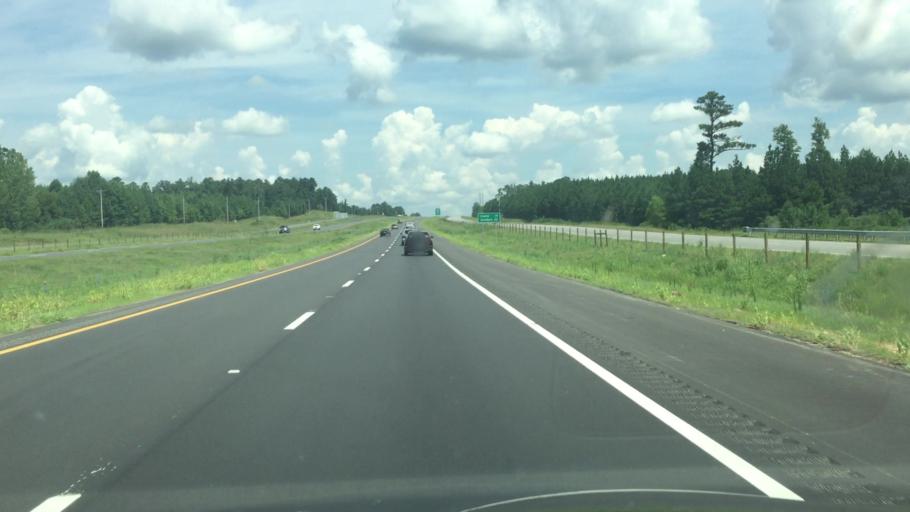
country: US
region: North Carolina
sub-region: Richmond County
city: Ellerbe
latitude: 35.0269
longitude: -79.7695
